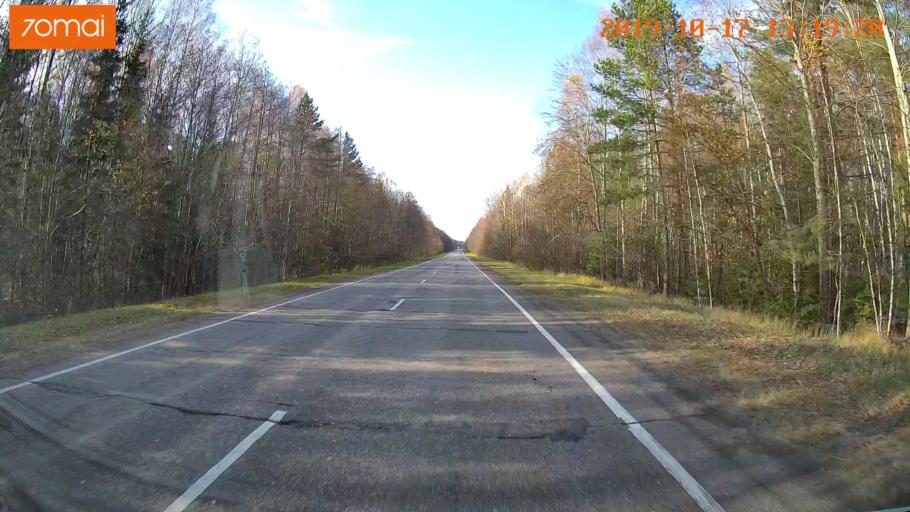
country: RU
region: Rjazan
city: Gus'-Zheleznyy
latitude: 55.0688
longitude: 41.0765
